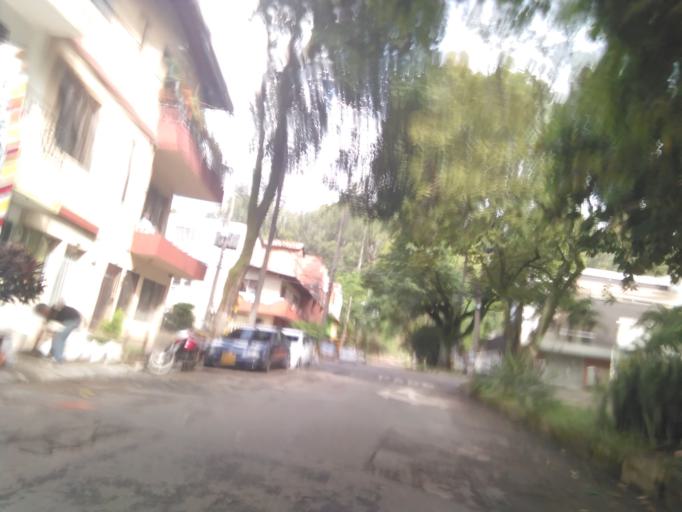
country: CO
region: Antioquia
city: Medellin
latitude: 6.2371
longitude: -75.5838
